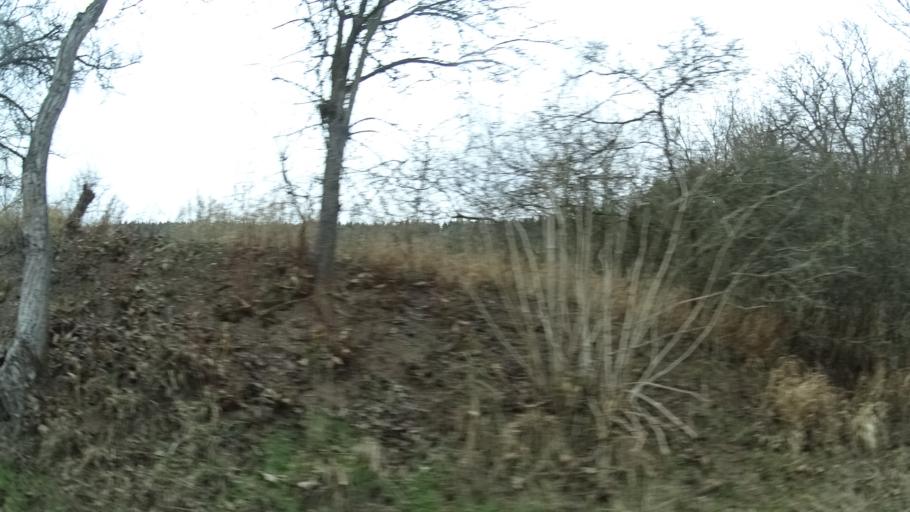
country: DE
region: Thuringia
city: Bad Blankenburg
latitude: 50.7050
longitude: 11.2310
